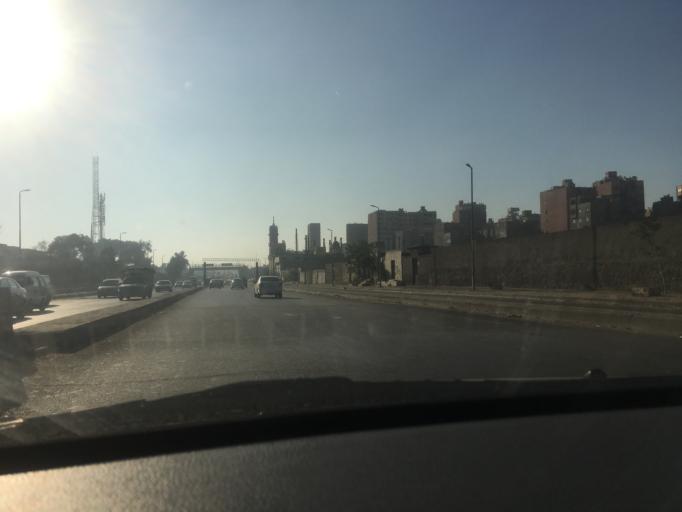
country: EG
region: Muhafazat al Qahirah
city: Cairo
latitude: 30.0160
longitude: 31.2654
